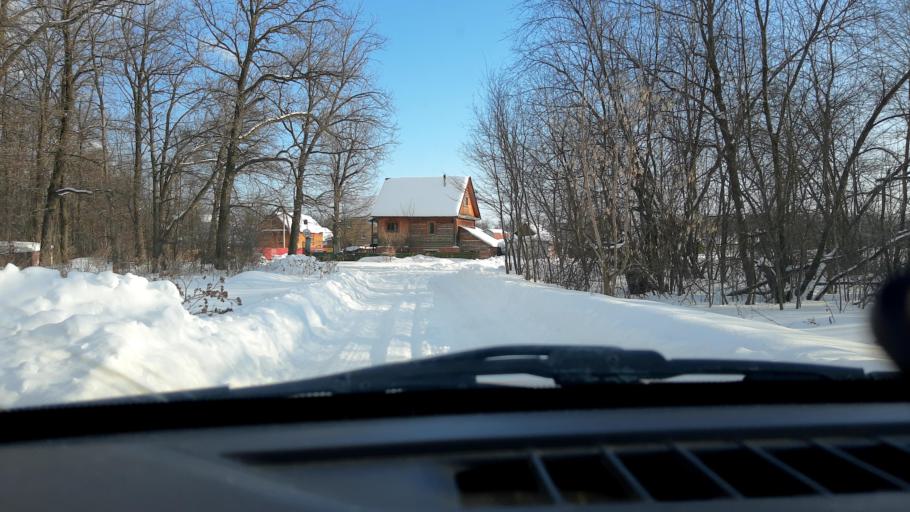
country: RU
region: Bashkortostan
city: Ufa
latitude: 54.6321
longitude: 56.0069
